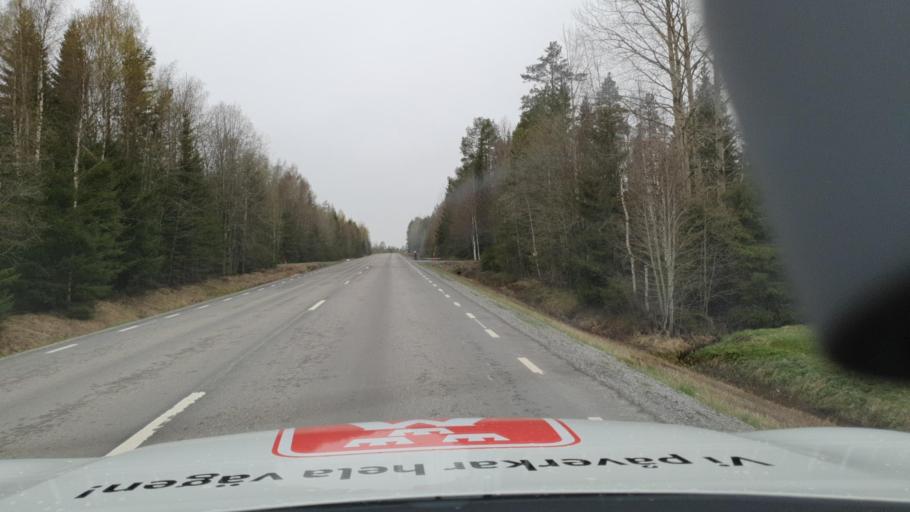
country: SE
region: Vaesterbotten
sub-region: Umea Kommun
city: Hoernefors
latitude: 63.7768
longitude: 19.8902
